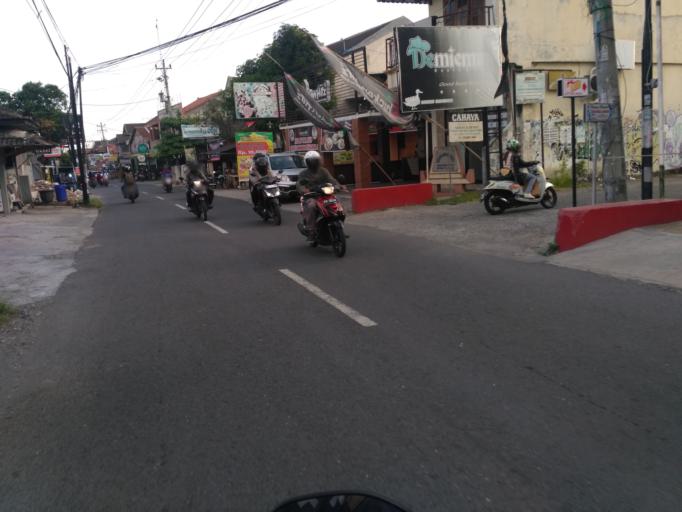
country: ID
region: Daerah Istimewa Yogyakarta
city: Depok
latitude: -7.7643
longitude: 110.4060
